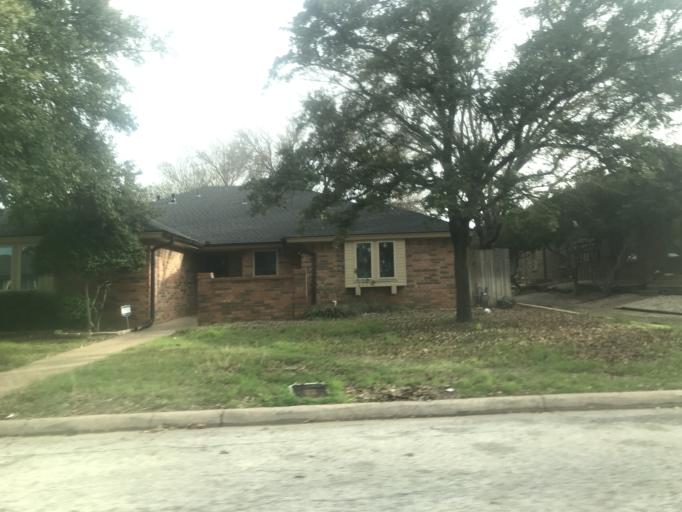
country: US
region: Texas
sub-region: Taylor County
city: Abilene
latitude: 32.3943
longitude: -99.7614
